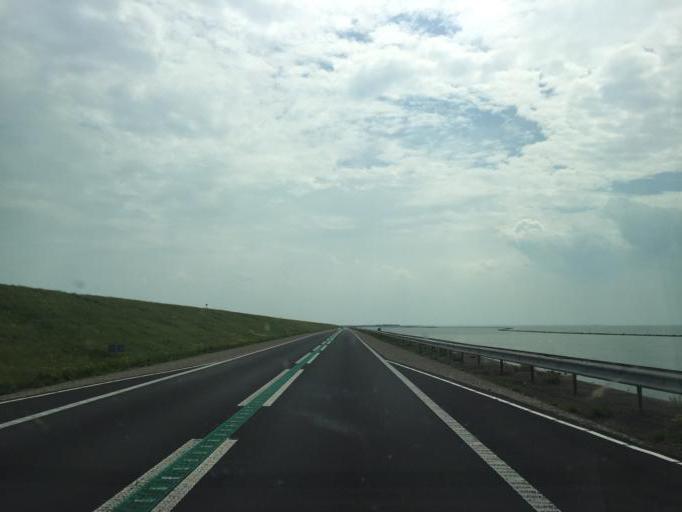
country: NL
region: North Holland
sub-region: Gemeente Enkhuizen
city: Enkhuizen
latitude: 52.6633
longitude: 5.3774
